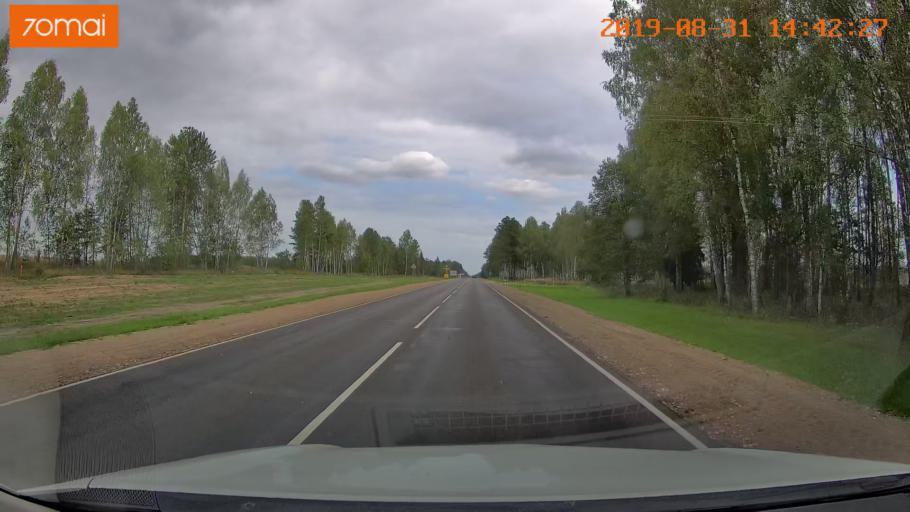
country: RU
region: Smolensk
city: Yekimovichi
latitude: 54.2082
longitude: 33.6088
